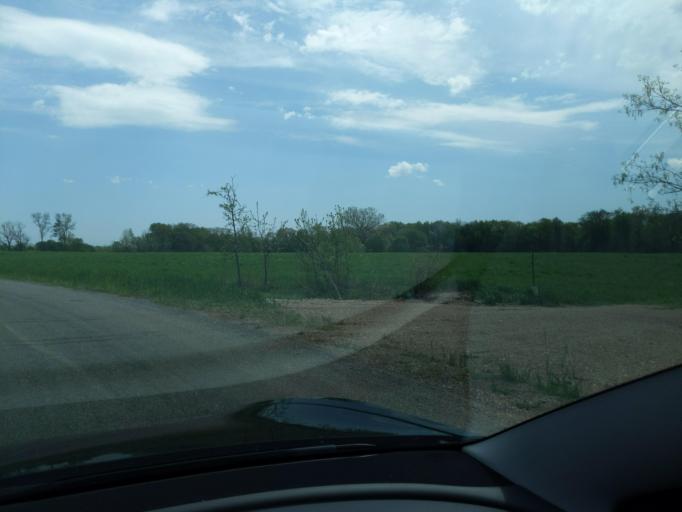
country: US
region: Michigan
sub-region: Ingham County
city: Stockbridge
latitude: 42.4687
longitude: -84.2283
